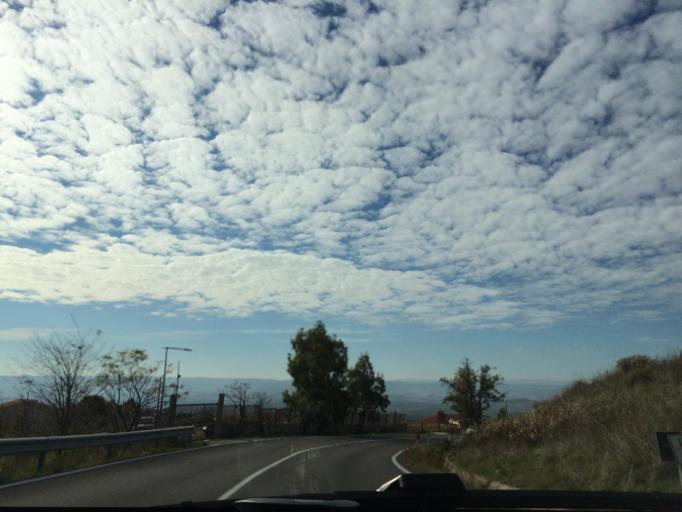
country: IT
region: Basilicate
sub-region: Provincia di Matera
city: Matera
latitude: 40.6486
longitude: 16.6058
